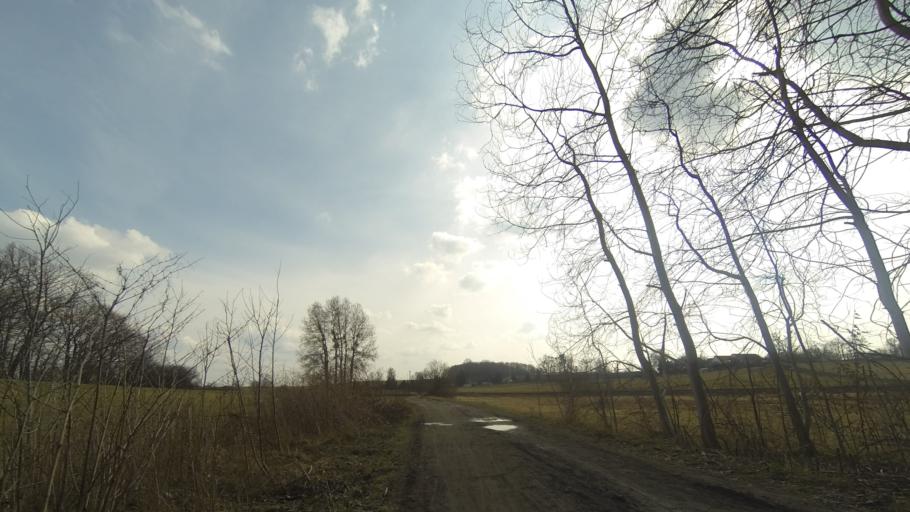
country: DE
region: Saxony
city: Moritzburg
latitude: 51.1636
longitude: 13.7127
